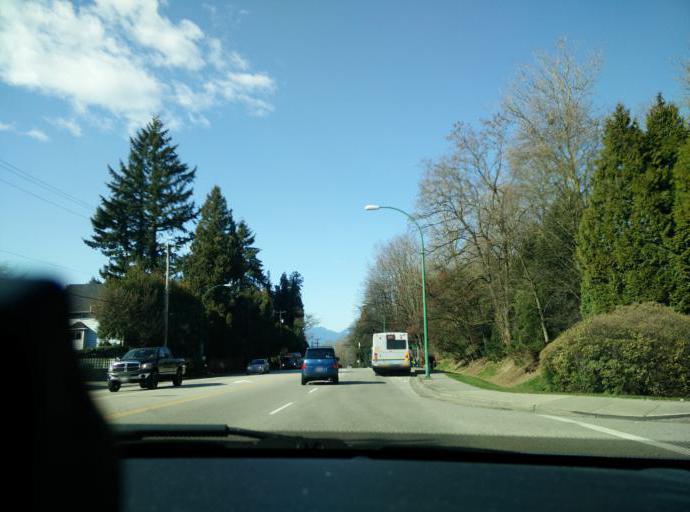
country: CA
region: British Columbia
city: Burnaby
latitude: 49.2357
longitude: -122.9546
